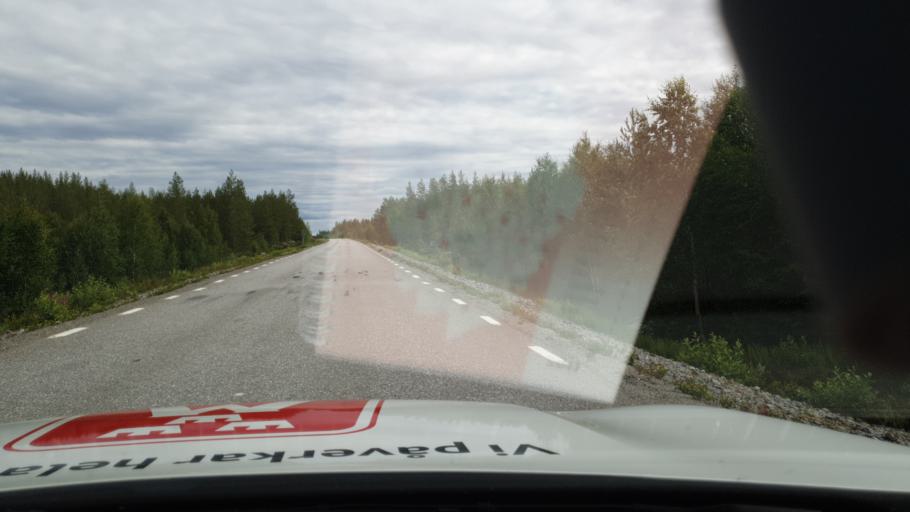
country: SE
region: Vaesterbotten
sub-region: Storumans Kommun
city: Storuman
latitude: 65.5038
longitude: 17.0325
